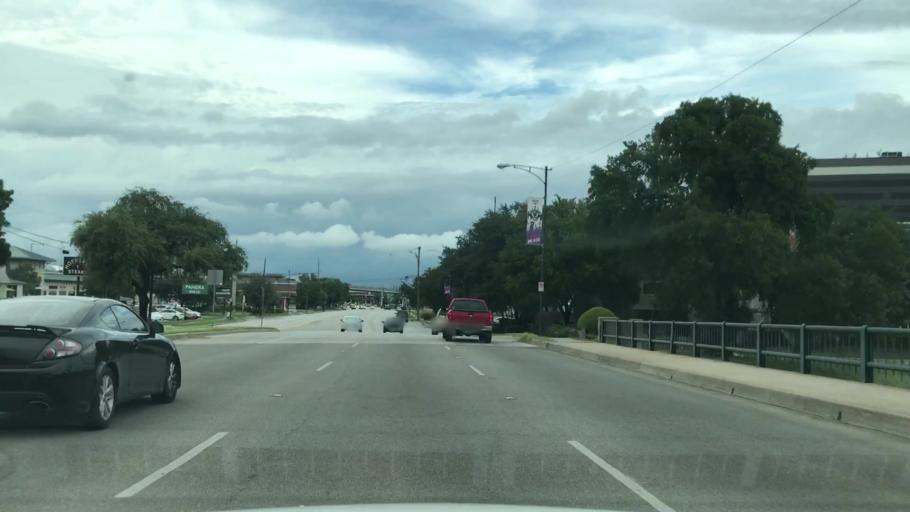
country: US
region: Texas
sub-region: Tarrant County
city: Fort Worth
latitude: 32.7248
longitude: -97.3611
